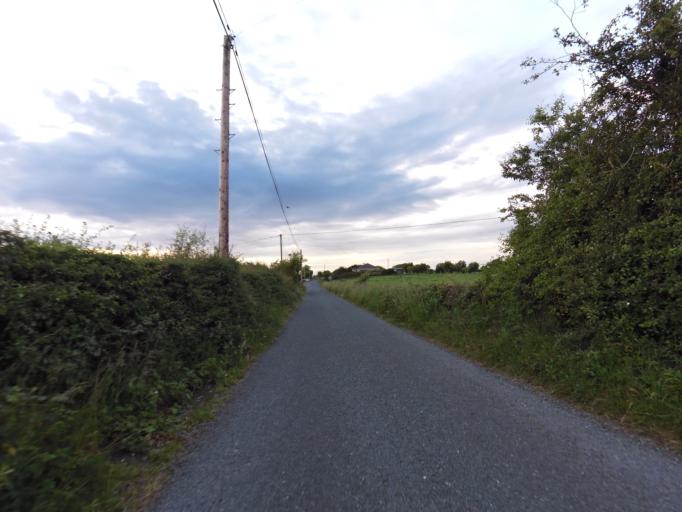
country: IE
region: Connaught
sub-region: County Galway
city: Athenry
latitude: 53.2882
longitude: -8.7130
